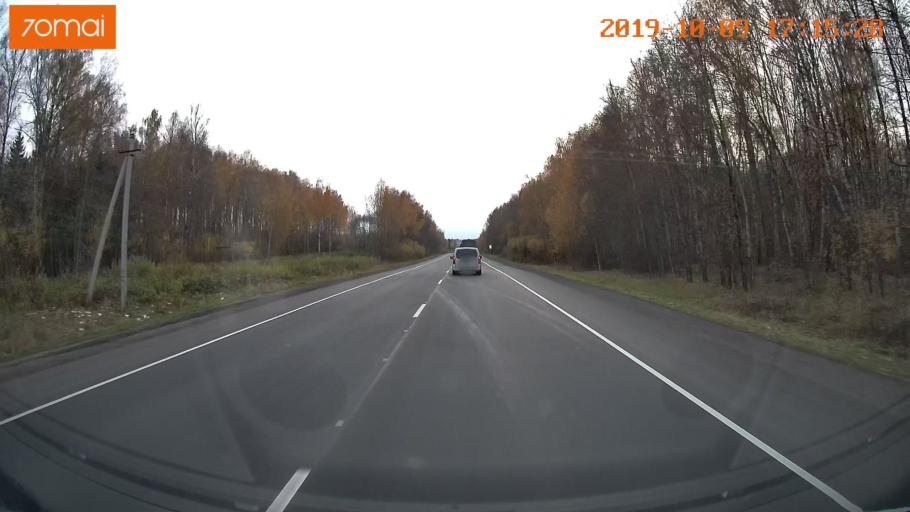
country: RU
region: Ivanovo
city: Furmanov
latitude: 57.2975
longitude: 41.1896
